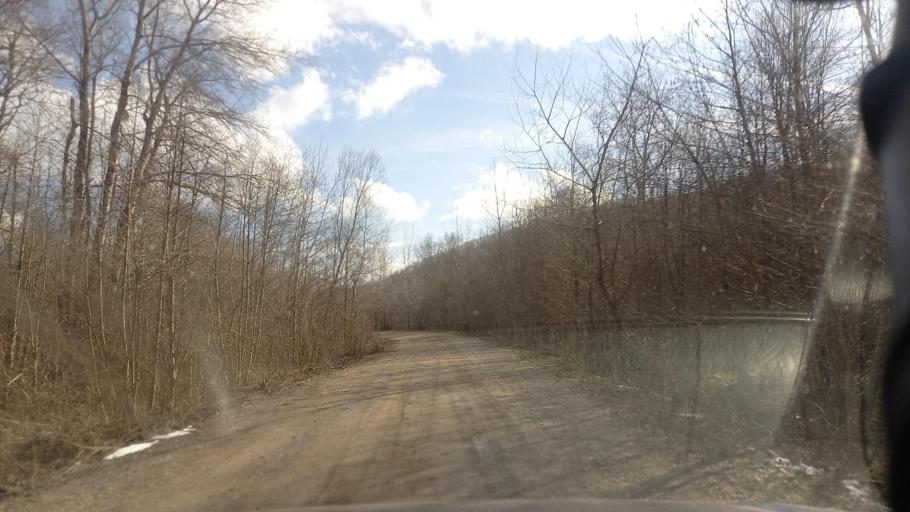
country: RU
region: Krasnodarskiy
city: Smolenskaya
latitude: 44.6187
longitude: 38.8264
